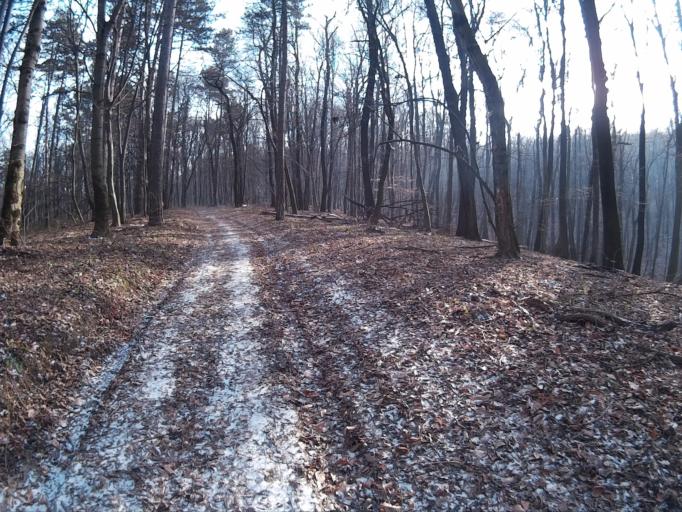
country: HU
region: Fejer
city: Szarliget
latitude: 47.4906
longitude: 18.4092
